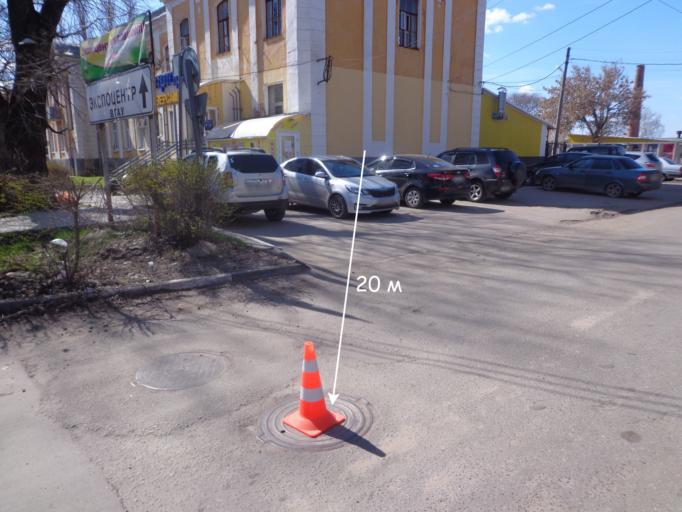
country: RU
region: Voronezj
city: Voronezh
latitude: 51.7140
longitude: 39.2234
